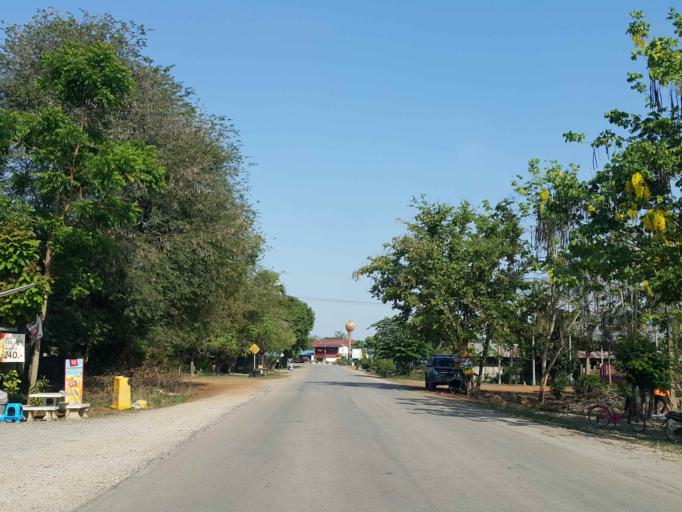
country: TH
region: Sukhothai
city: Thung Saliam
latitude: 17.3271
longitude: 99.6213
